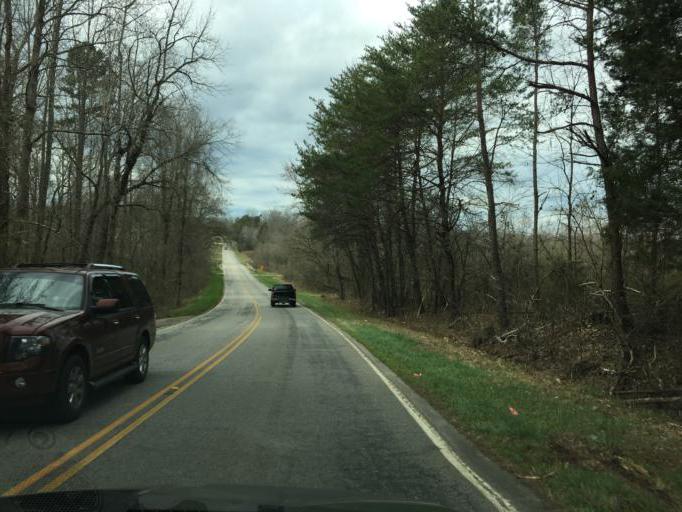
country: US
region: South Carolina
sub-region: Greenville County
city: Golden Grove
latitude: 34.7002
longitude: -82.4231
